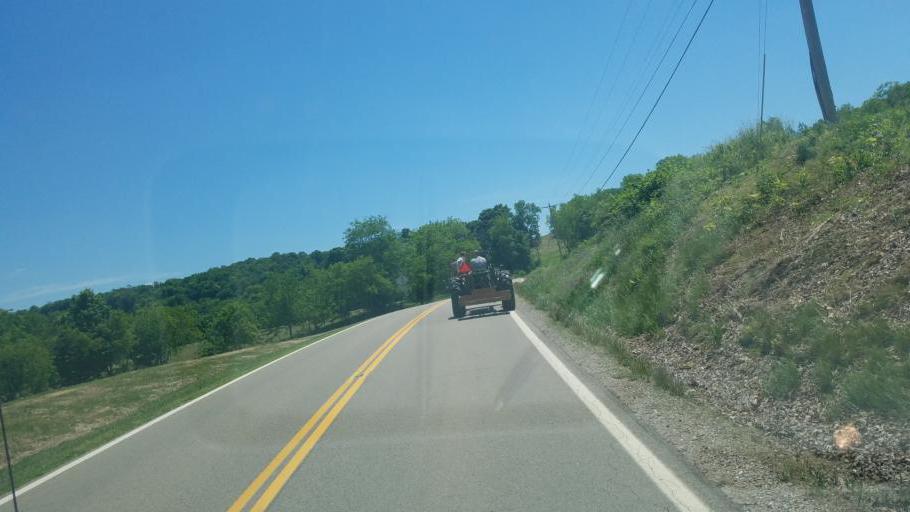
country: US
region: Ohio
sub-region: Coshocton County
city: Coshocton
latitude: 40.3093
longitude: -82.0138
